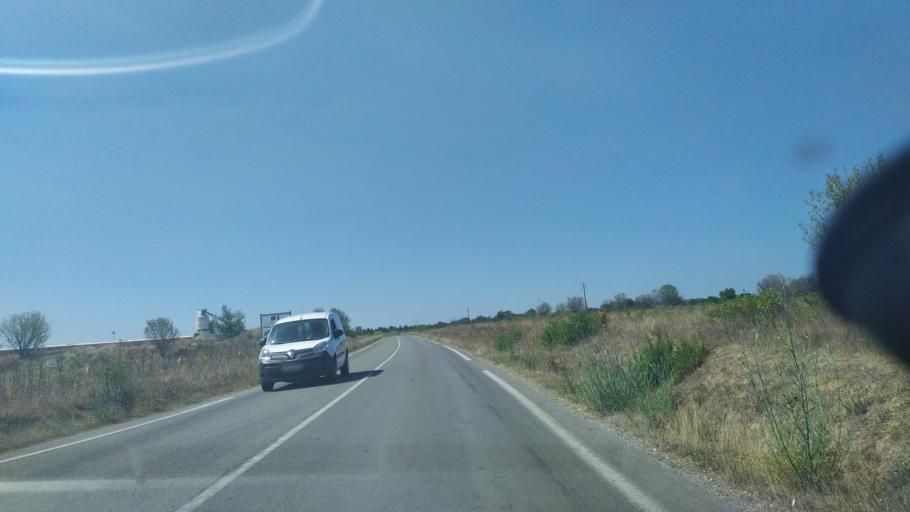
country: FR
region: Languedoc-Roussillon
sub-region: Departement du Gard
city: Codognan
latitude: 43.7211
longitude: 4.2251
